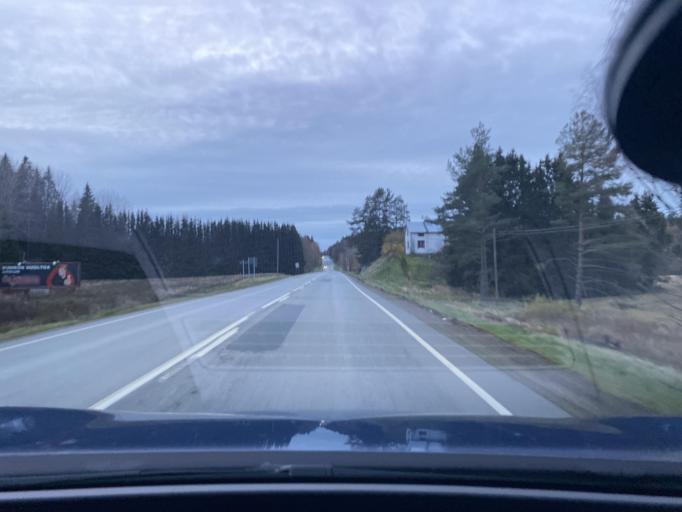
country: FI
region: Uusimaa
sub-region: Helsinki
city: Sammatti
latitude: 60.3845
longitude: 23.8803
